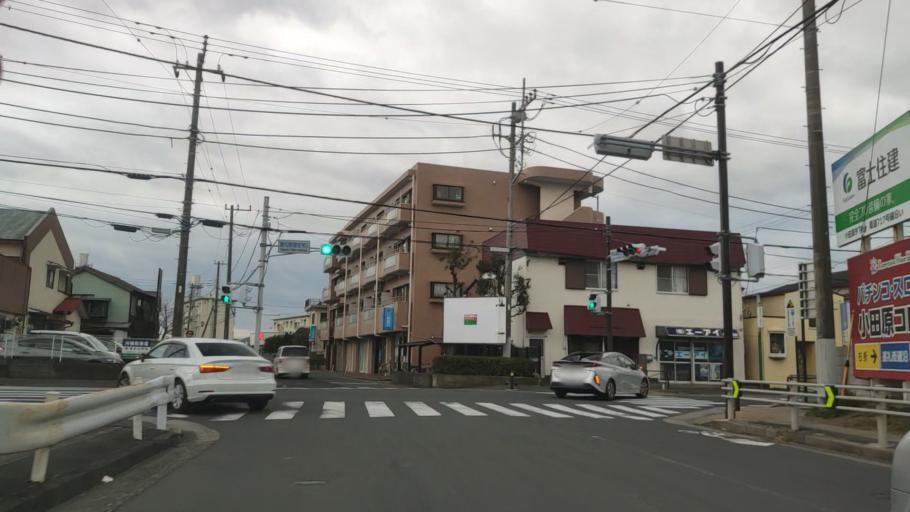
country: JP
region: Kanagawa
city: Odawara
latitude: 35.2672
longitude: 139.1899
